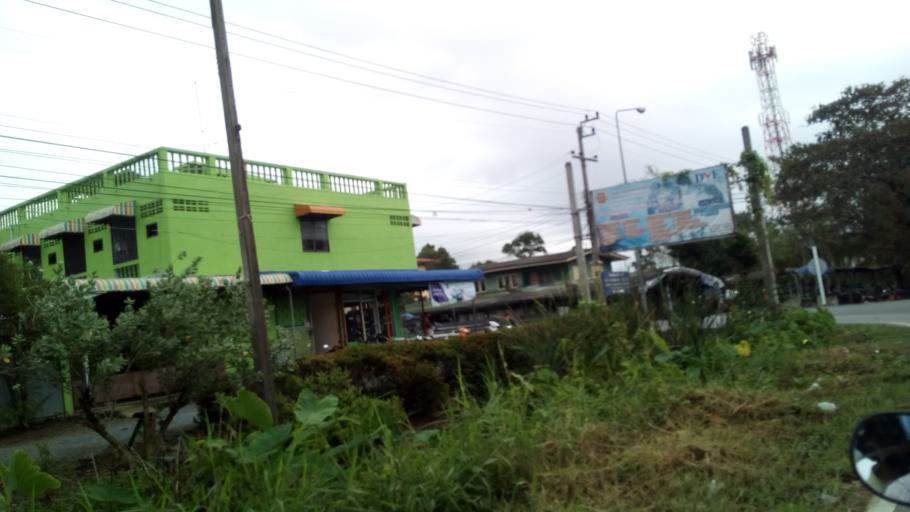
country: TH
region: Pathum Thani
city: Nong Suea
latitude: 14.0732
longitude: 100.8884
